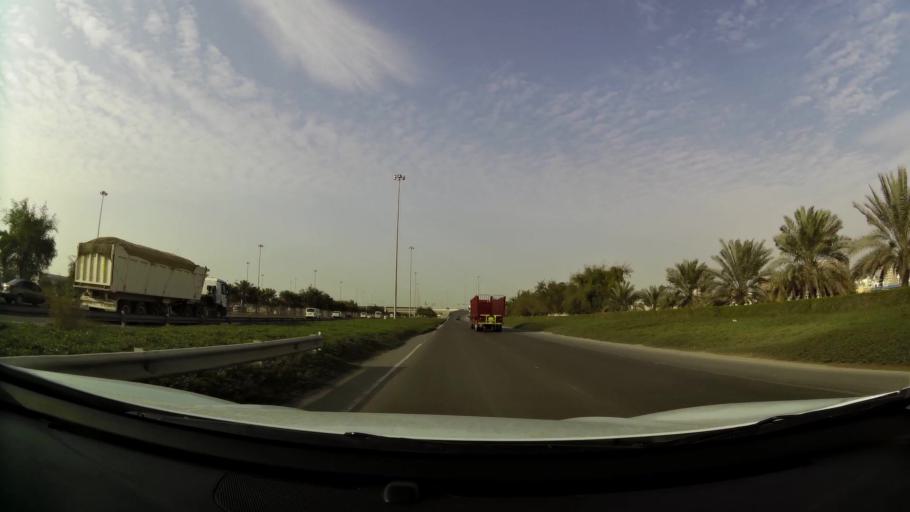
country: AE
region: Abu Dhabi
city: Abu Dhabi
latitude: 24.3196
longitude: 54.5270
